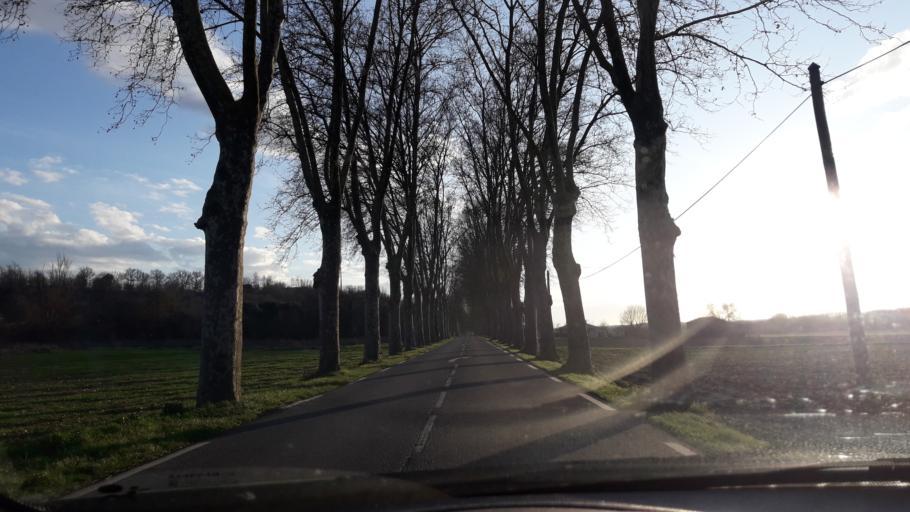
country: FR
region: Midi-Pyrenees
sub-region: Departement de la Haute-Garonne
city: Grenade
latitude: 43.7393
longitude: 1.2625
